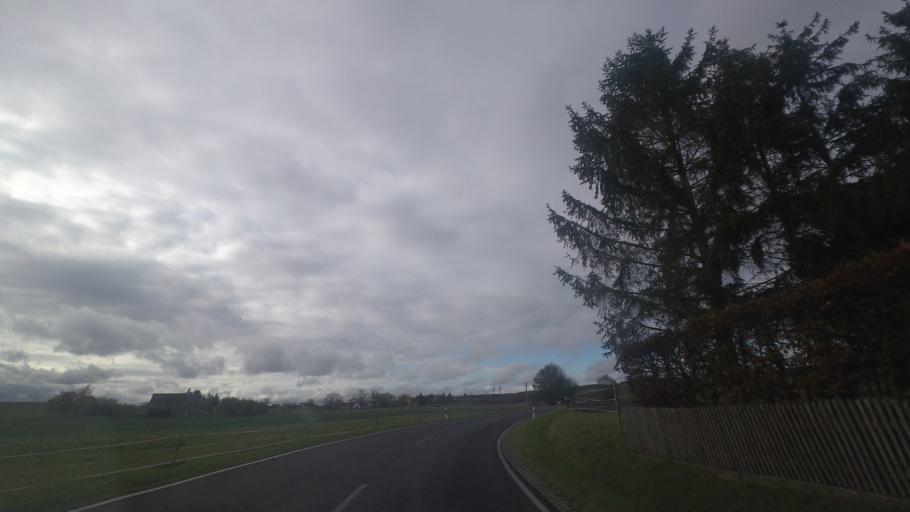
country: DE
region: Bavaria
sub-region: Regierungsbezirk Unterfranken
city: Hochheim
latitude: 50.3912
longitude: 10.4879
